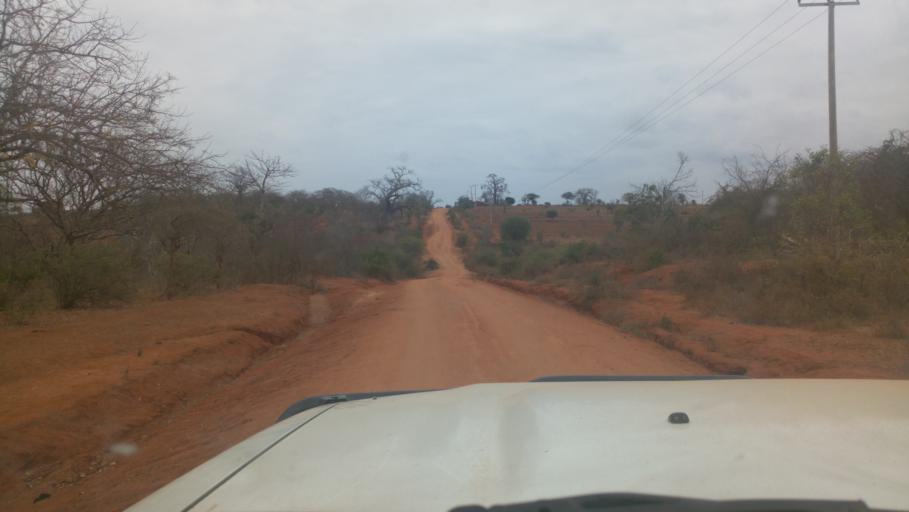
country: KE
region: Makueni
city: Makueni
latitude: -2.0226
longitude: 38.1013
